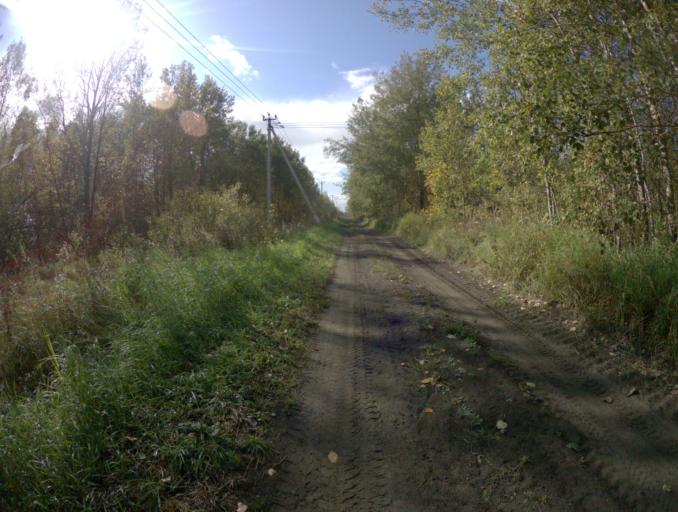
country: RU
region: Moskovskaya
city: Kerva
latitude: 55.7056
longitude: 39.5908
